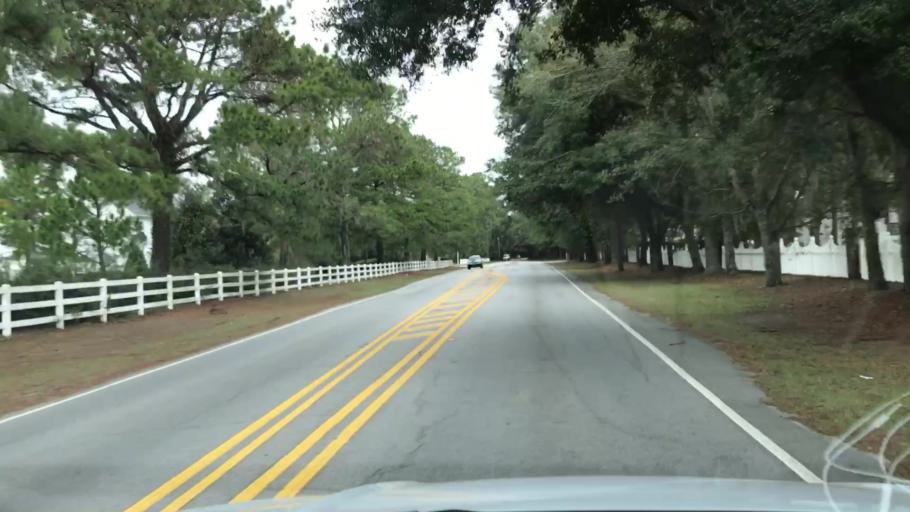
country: US
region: South Carolina
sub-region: Beaufort County
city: Bluffton
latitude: 32.2712
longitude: -80.8782
